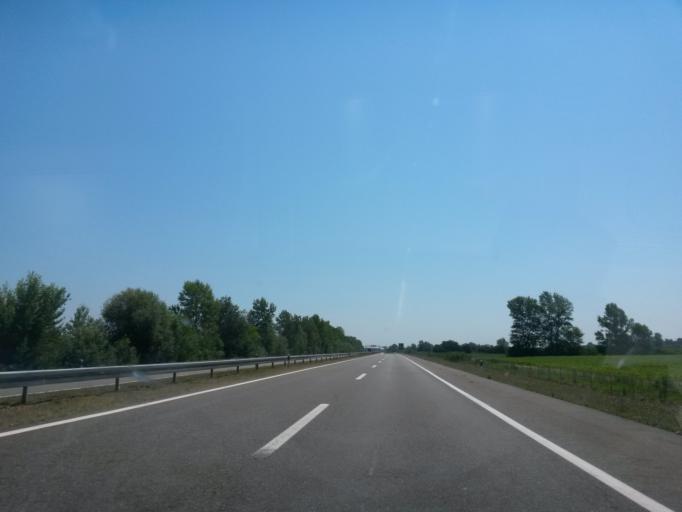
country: BA
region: Federation of Bosnia and Herzegovina
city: Donja Dubica
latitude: 45.1360
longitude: 18.3836
